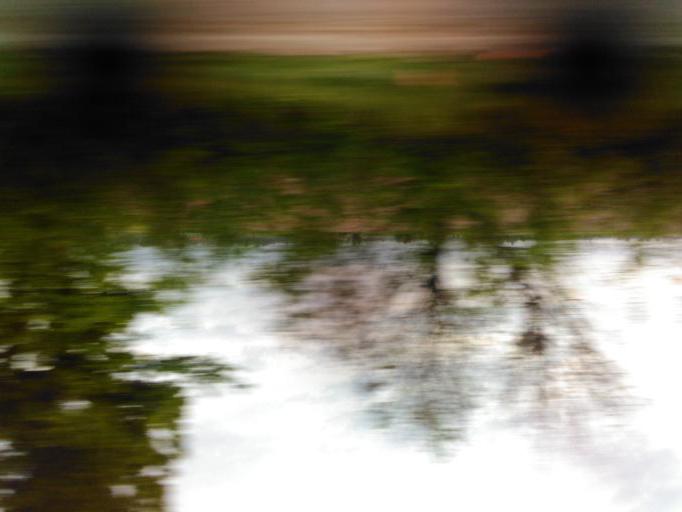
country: KG
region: Chuy
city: Bishkek
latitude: 42.9360
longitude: 74.5033
